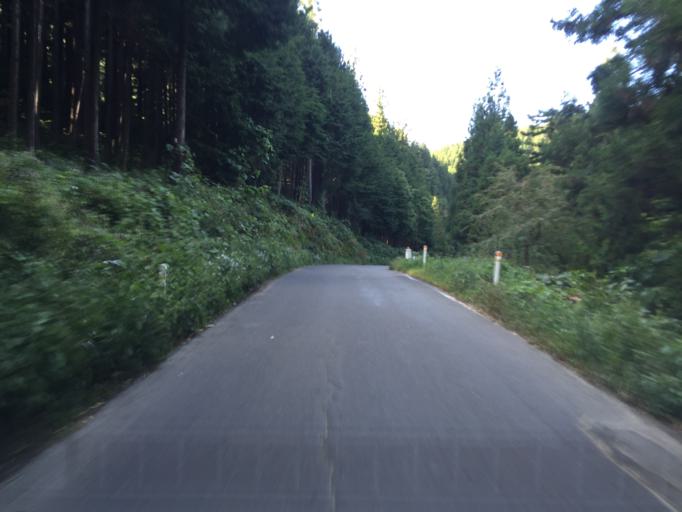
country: JP
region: Miyagi
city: Marumori
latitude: 37.8465
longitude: 140.7423
